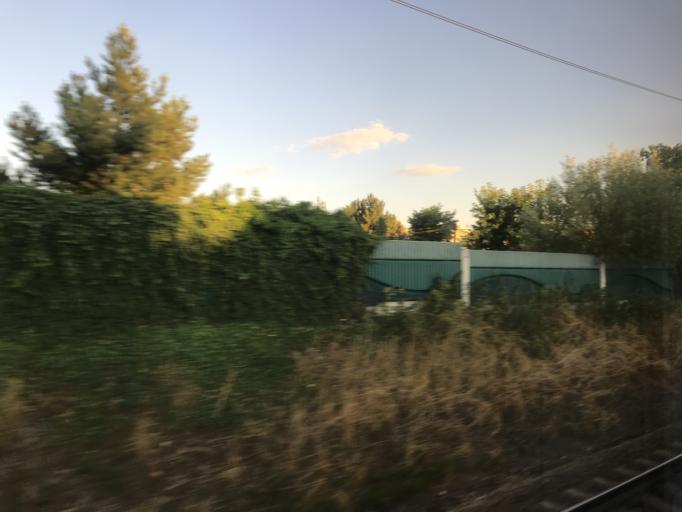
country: CZ
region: Central Bohemia
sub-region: Okres Benesov
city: Benesov
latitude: 49.7908
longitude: 14.6948
